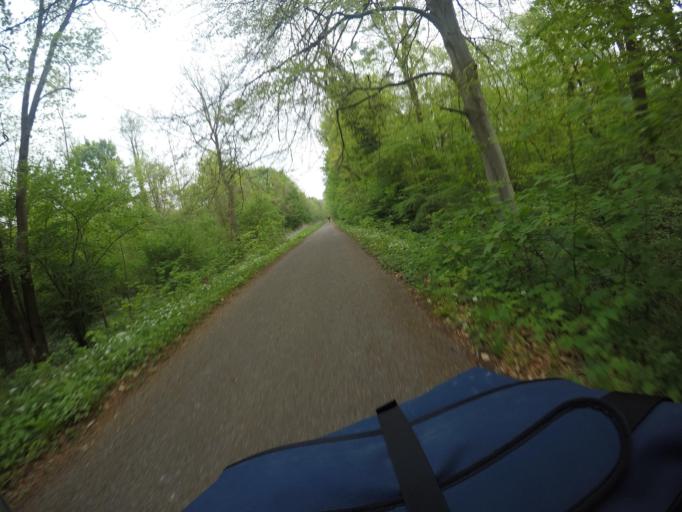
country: DE
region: Baden-Wuerttemberg
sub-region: Freiburg Region
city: Kehl
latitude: 48.6136
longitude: 7.8196
